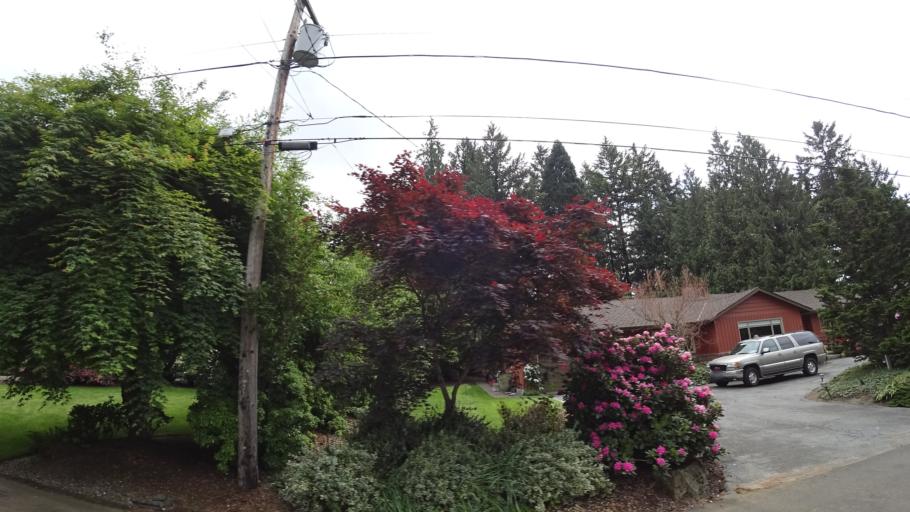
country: US
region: Oregon
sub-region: Washington County
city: Cedar Hills
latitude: 45.4991
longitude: -122.7836
